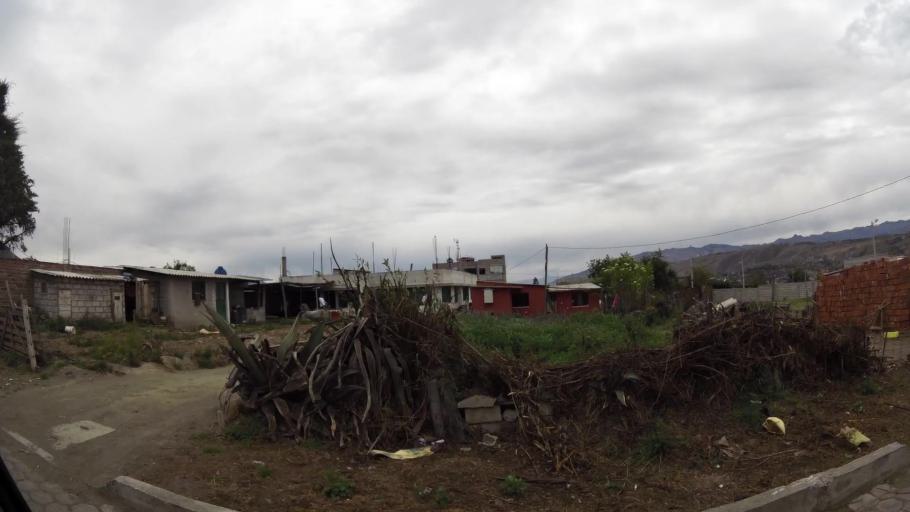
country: EC
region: Cotopaxi
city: Latacunga
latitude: -0.9613
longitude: -78.6081
